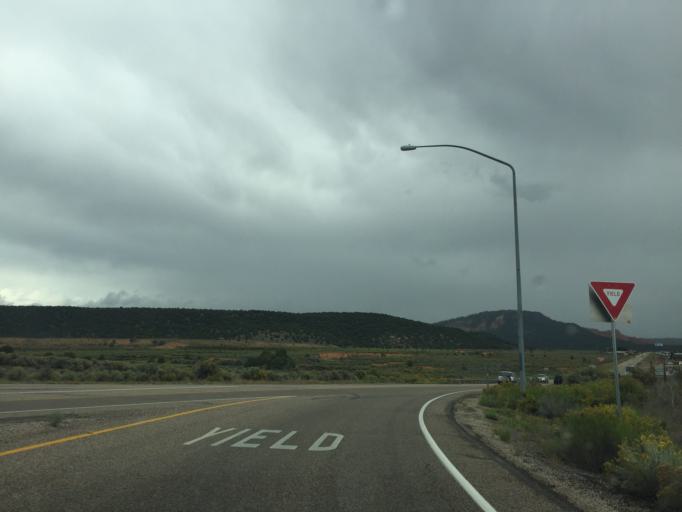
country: US
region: Utah
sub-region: Garfield County
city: Panguitch
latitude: 37.7495
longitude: -112.3765
